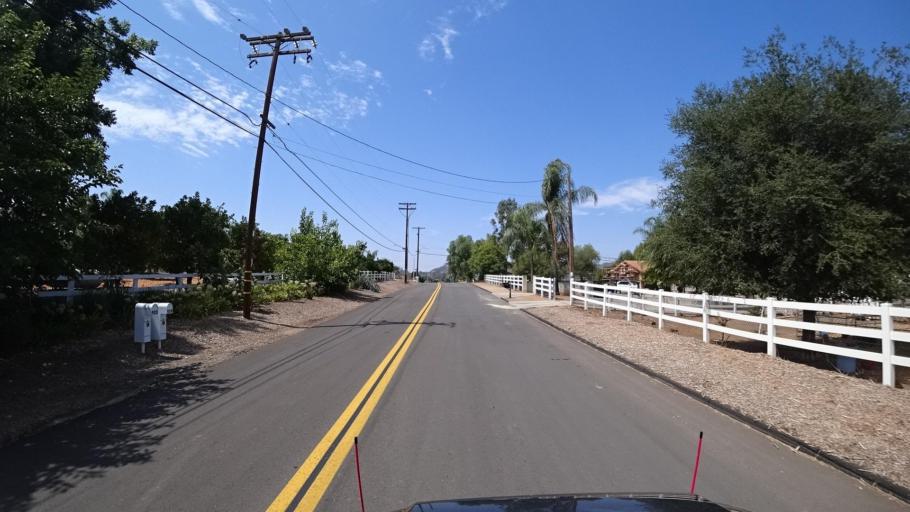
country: US
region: California
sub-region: San Diego County
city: Escondido
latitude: 33.1754
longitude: -117.0826
